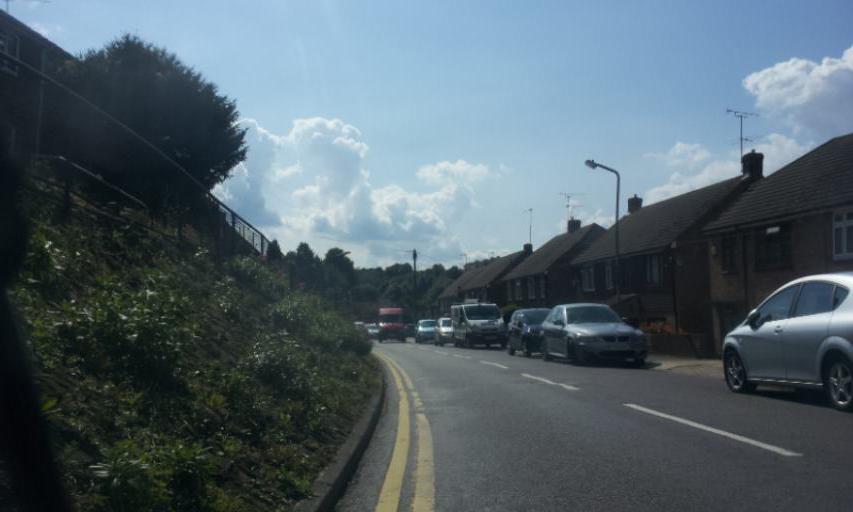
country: GB
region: England
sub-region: Kent
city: Chatham
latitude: 51.3475
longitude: 0.5145
